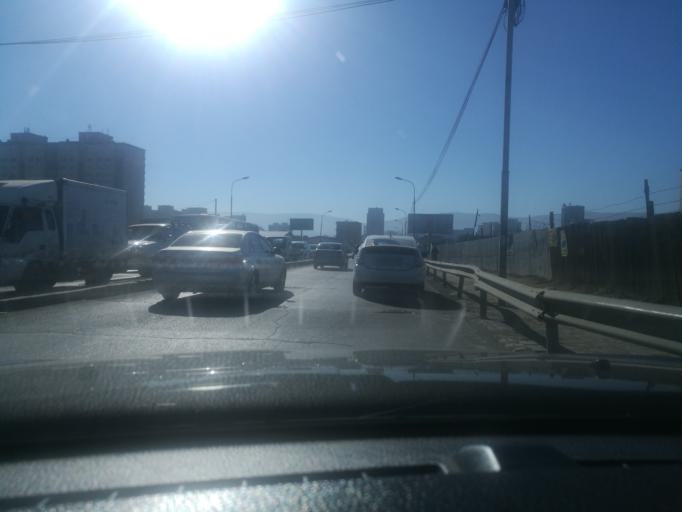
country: MN
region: Ulaanbaatar
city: Ulaanbaatar
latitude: 47.9396
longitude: 106.9150
